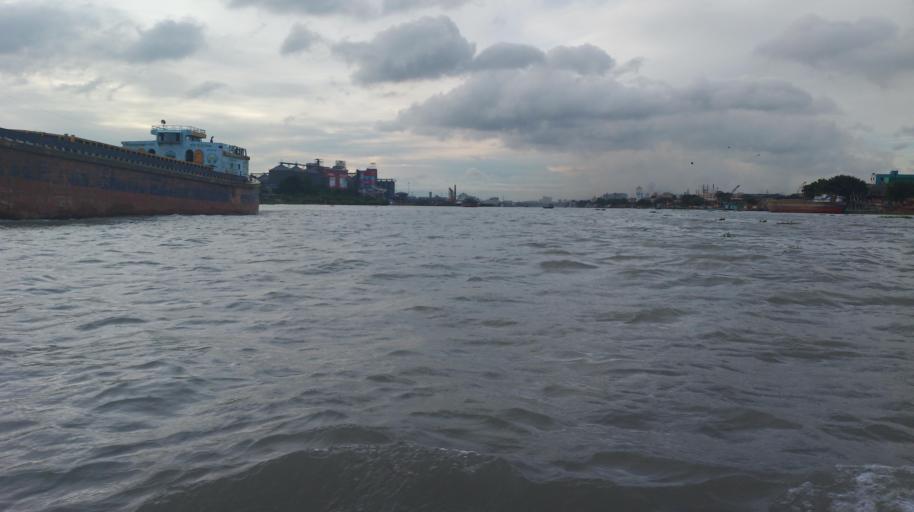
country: BD
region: Dhaka
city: Narayanganj
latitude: 23.6606
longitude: 90.4548
